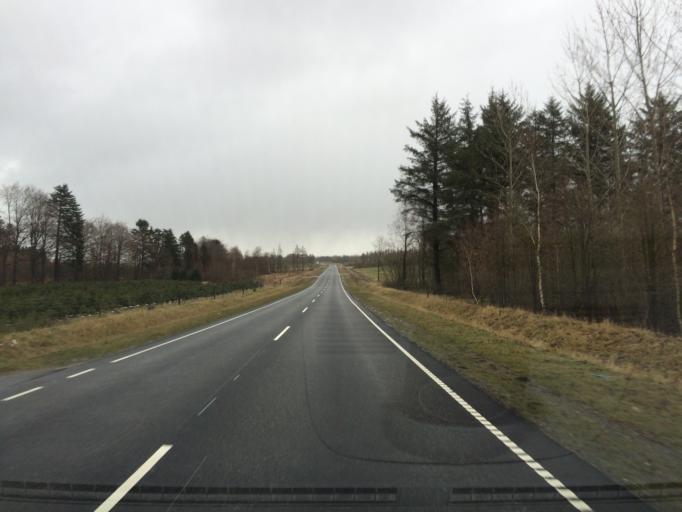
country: DK
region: Central Jutland
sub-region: Herning Kommune
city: Vildbjerg
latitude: 56.1825
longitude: 8.6756
